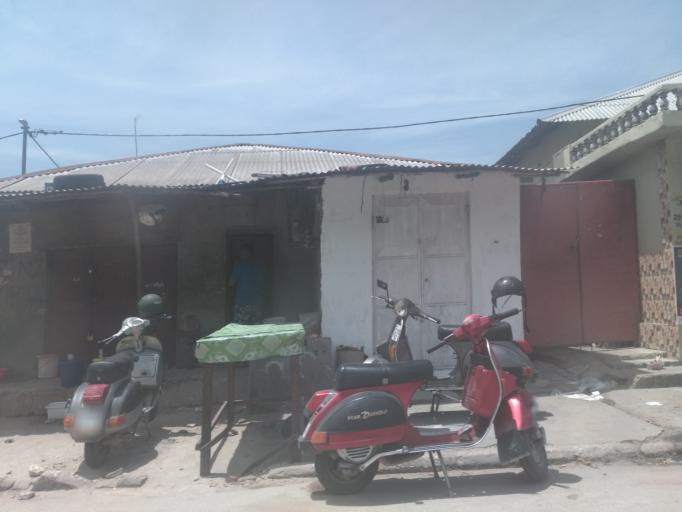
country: TZ
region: Zanzibar Urban/West
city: Zanzibar
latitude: -6.1597
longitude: 39.2042
